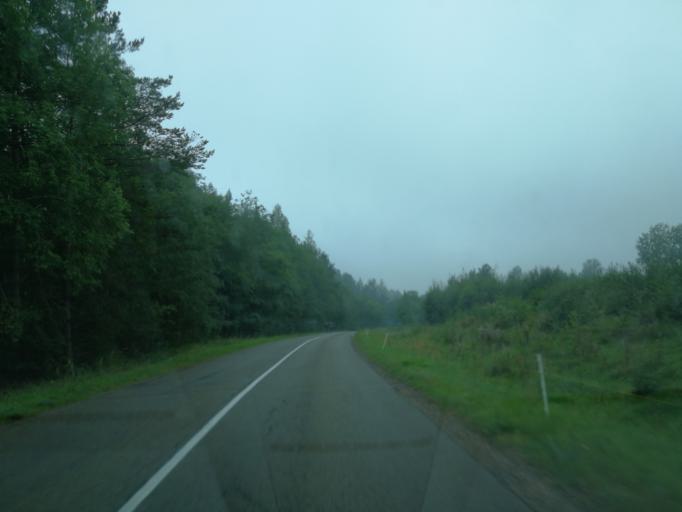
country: LV
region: Preilu Rajons
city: Jaunaglona
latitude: 56.2622
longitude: 27.0172
